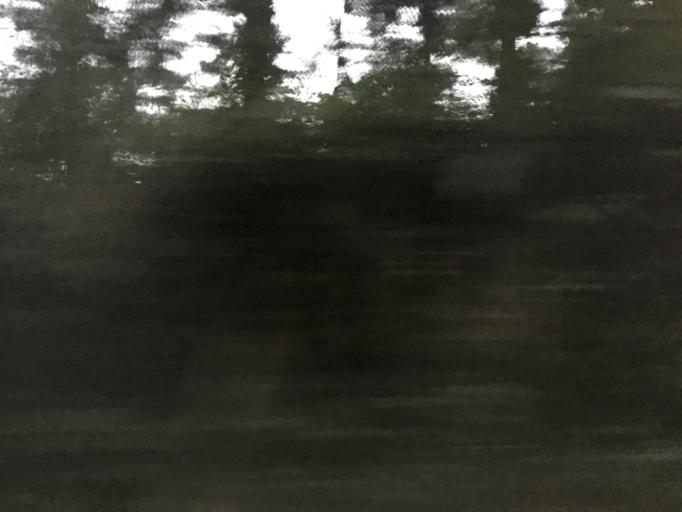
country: TW
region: Taiwan
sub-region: Chiayi
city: Jiayi Shi
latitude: 23.5059
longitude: 120.6605
